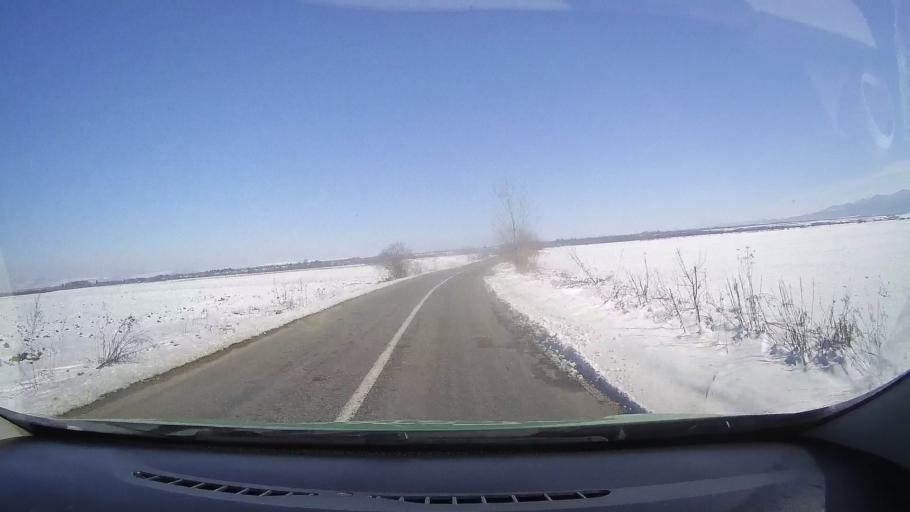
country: RO
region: Brasov
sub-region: Comuna Harseni
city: Harseni
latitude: 45.7289
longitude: 24.9847
